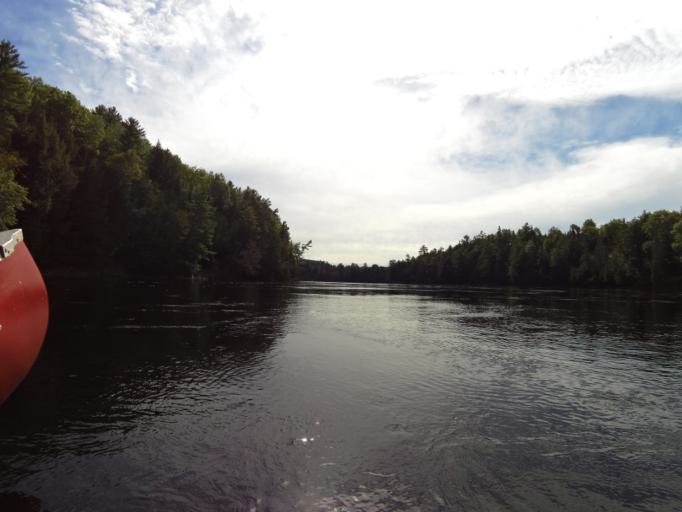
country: CA
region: Quebec
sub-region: Outaouais
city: Wakefield
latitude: 45.7802
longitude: -75.9436
